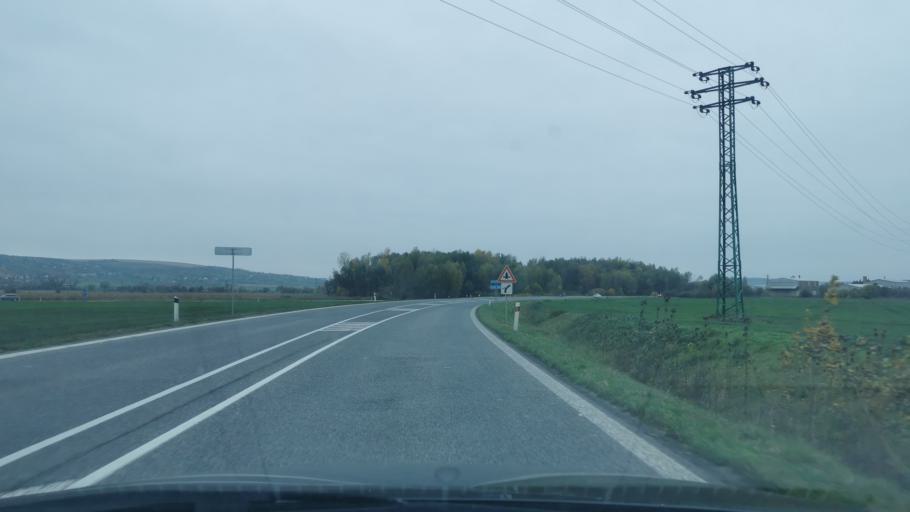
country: SK
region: Trnavsky
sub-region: Okres Skalica
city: Skalica
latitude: 48.8383
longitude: 17.2085
